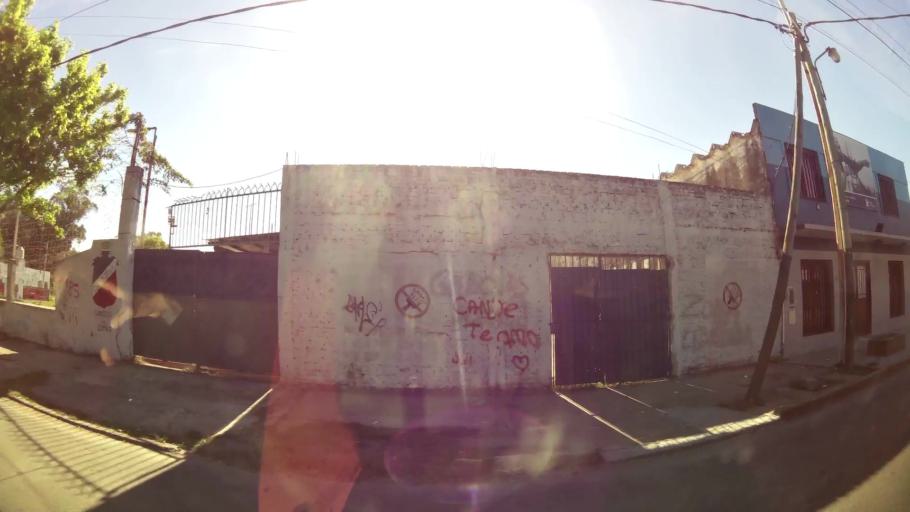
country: AR
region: Buenos Aires
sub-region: Partido de Lomas de Zamora
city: Lomas de Zamora
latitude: -34.7726
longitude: -58.4238
